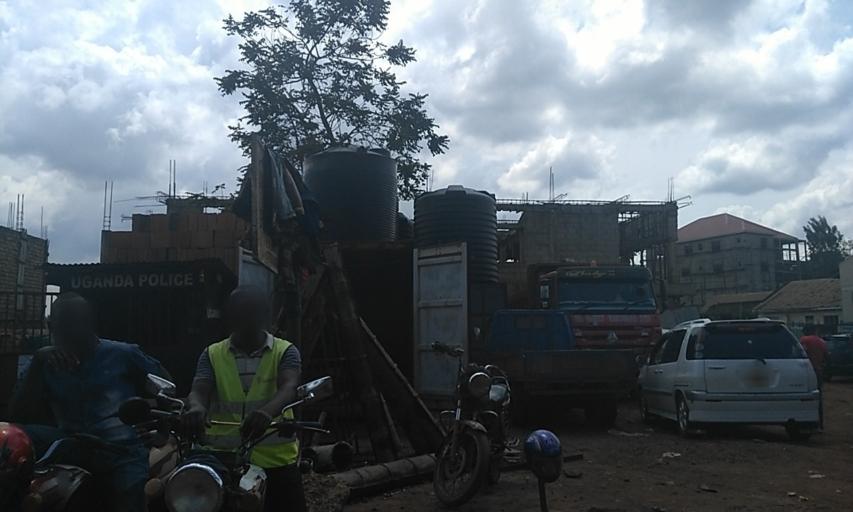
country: UG
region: Central Region
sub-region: Wakiso District
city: Wakiso
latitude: 0.3981
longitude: 32.4788
